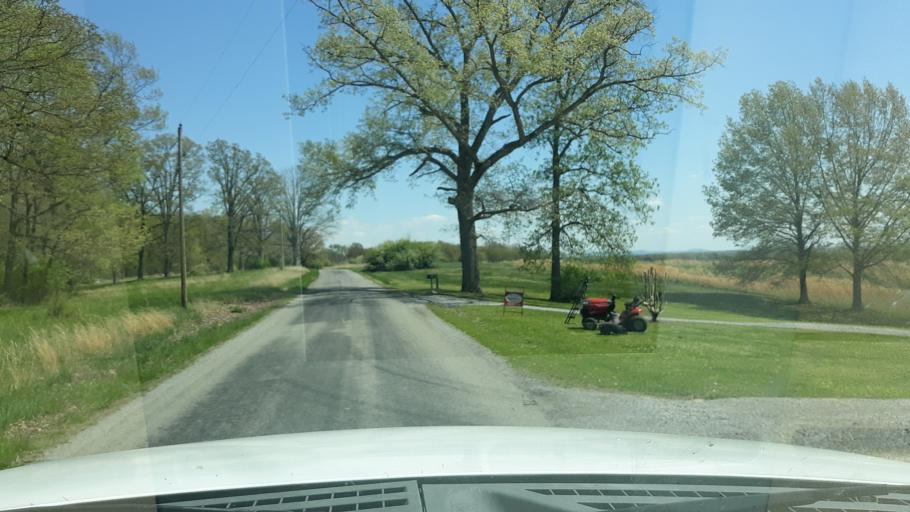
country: US
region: Illinois
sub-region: Saline County
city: Harrisburg
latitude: 37.8568
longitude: -88.6376
